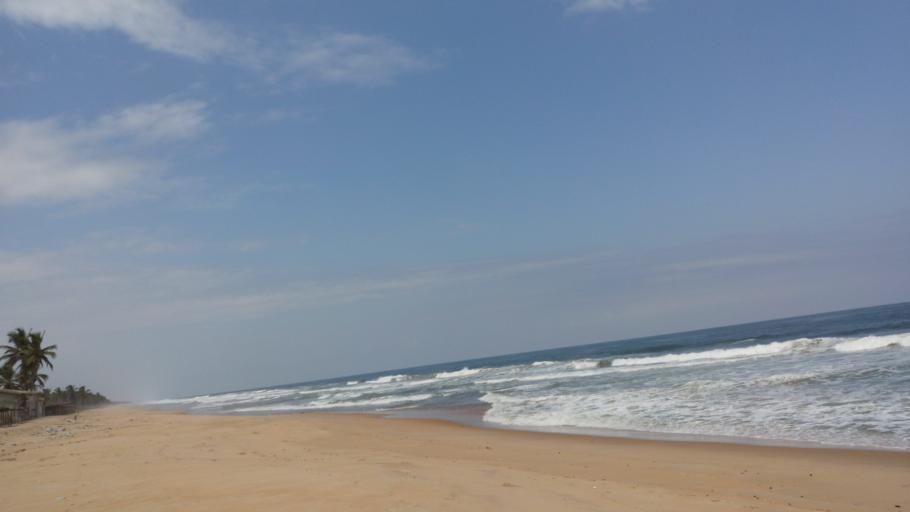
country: CI
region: Sud-Comoe
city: Grand-Bassam
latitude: 5.1868
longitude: -3.6887
